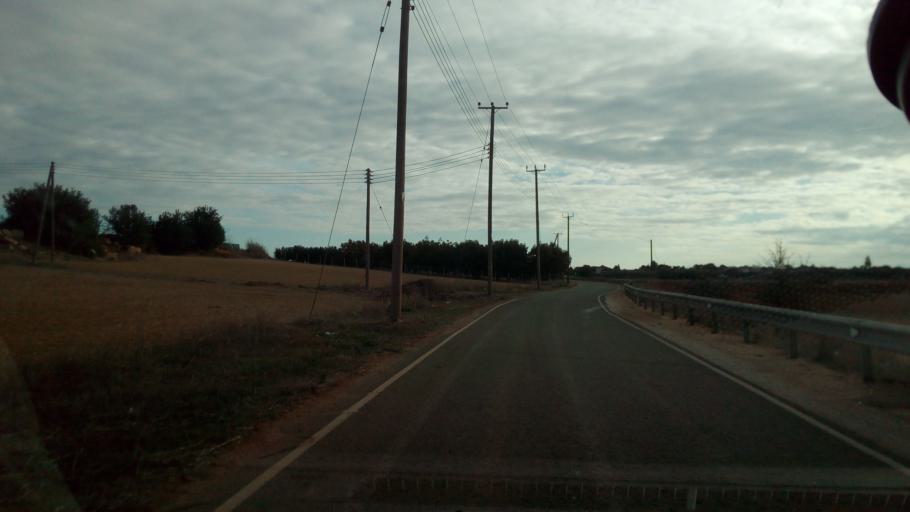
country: CY
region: Ammochostos
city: Frenaros
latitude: 35.0455
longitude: 33.8873
